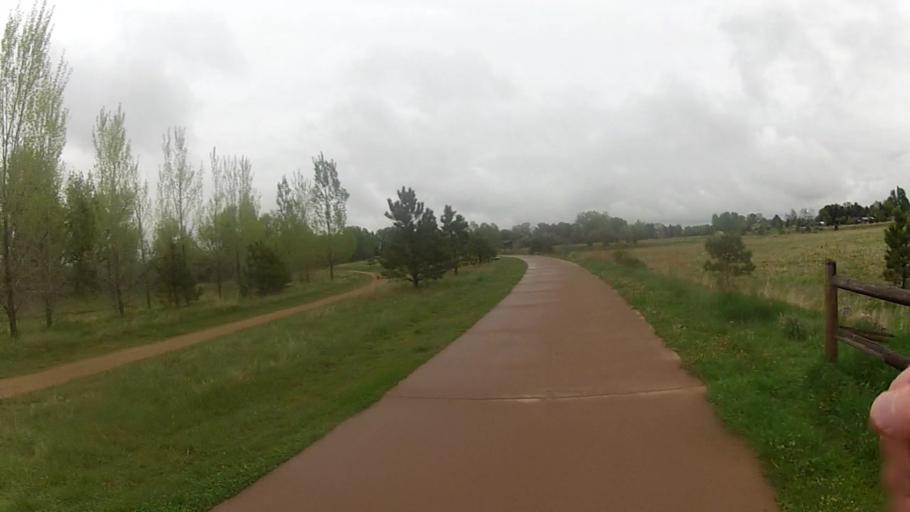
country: US
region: Colorado
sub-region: Larimer County
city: Fort Collins
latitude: 40.5448
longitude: -105.1271
